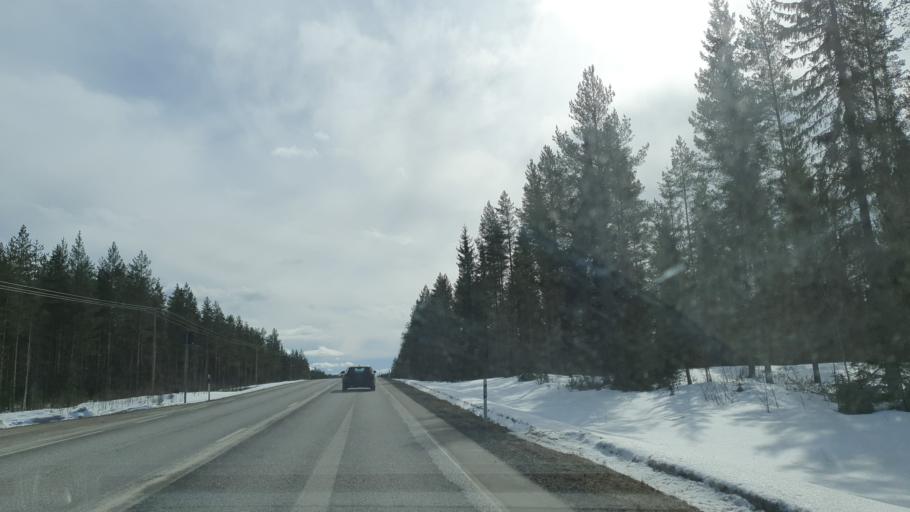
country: FI
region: Kainuu
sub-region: Kajaani
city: Ristijaervi
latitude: 64.3587
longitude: 28.0496
